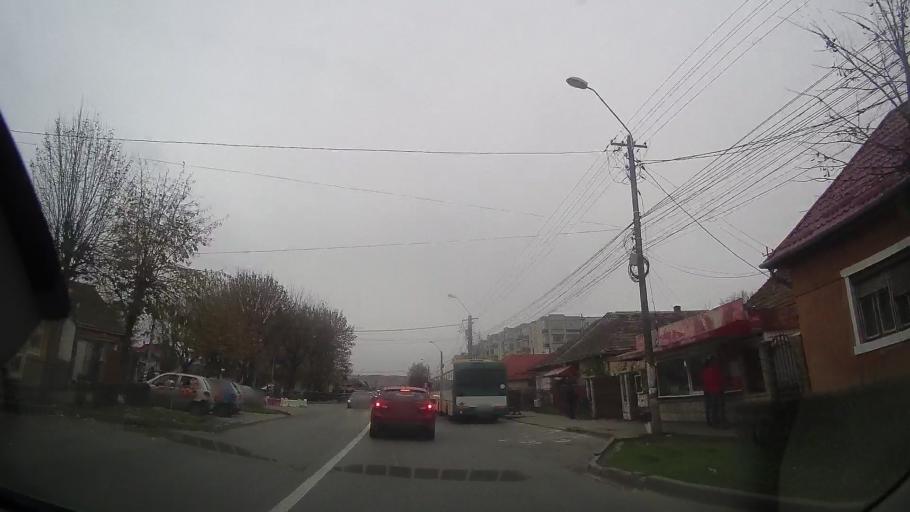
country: RO
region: Mures
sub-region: Comuna Santana de Mures
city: Santana de Mures
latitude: 46.5731
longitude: 24.5511
